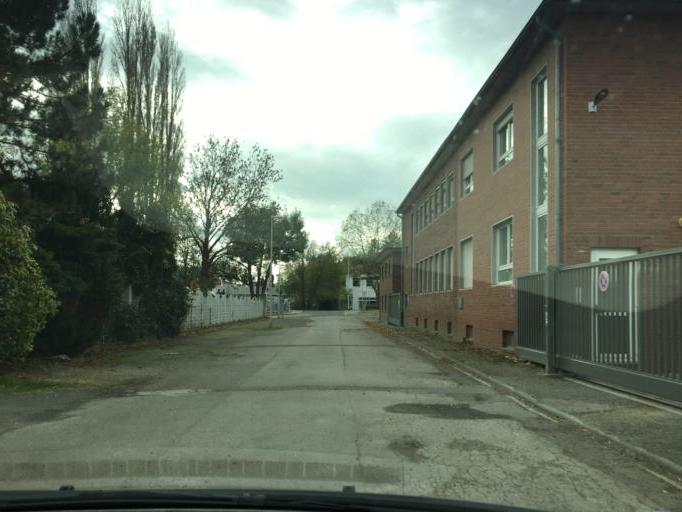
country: DE
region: North Rhine-Westphalia
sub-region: Regierungsbezirk Koln
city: Dueren
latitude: 50.7904
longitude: 6.4690
